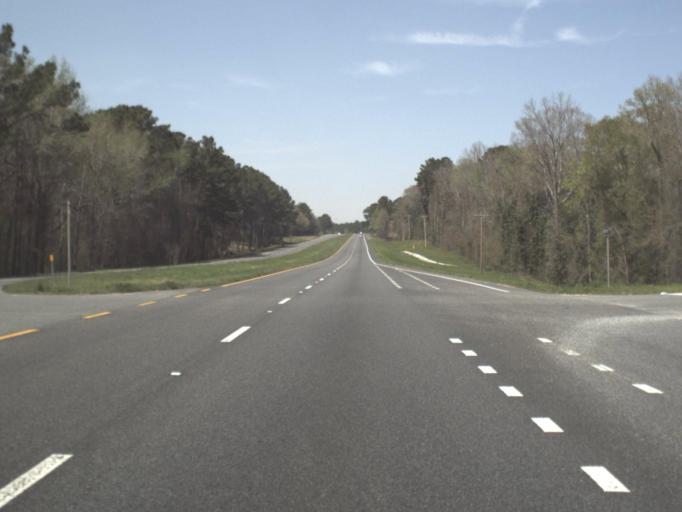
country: US
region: Florida
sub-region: Gadsden County
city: Midway
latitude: 30.5278
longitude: -84.4715
